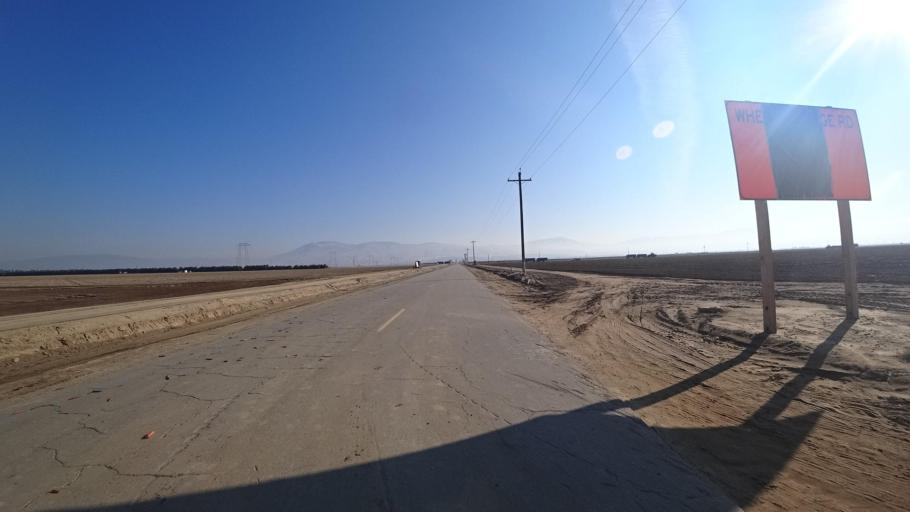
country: US
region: California
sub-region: Kern County
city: Weedpatch
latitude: 35.1219
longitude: -118.9193
